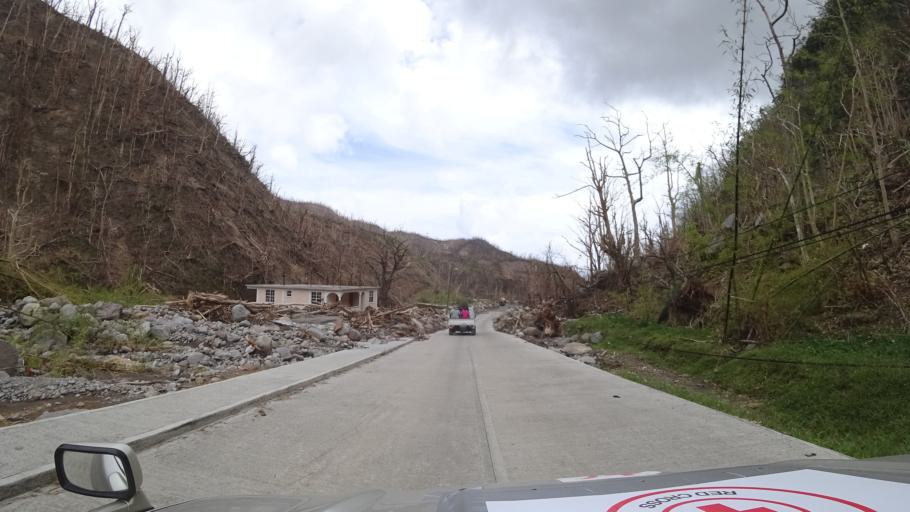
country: DM
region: Saint Patrick
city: Berekua
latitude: 15.2637
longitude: -61.3205
